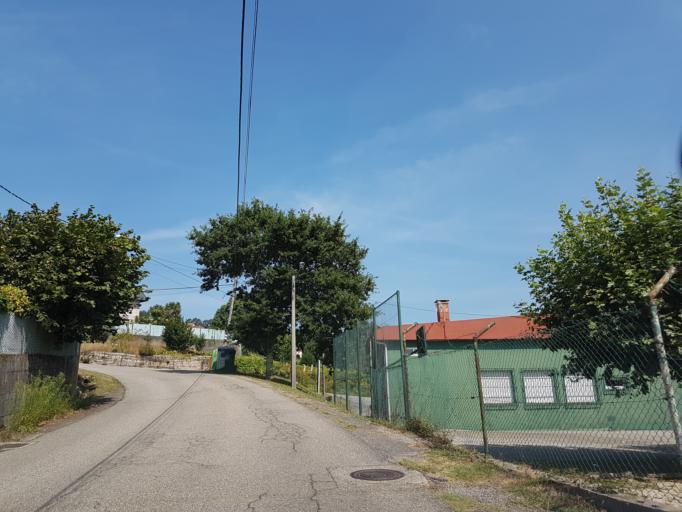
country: ES
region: Galicia
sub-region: Provincia de Pontevedra
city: Porrino
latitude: 42.2194
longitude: -8.6203
